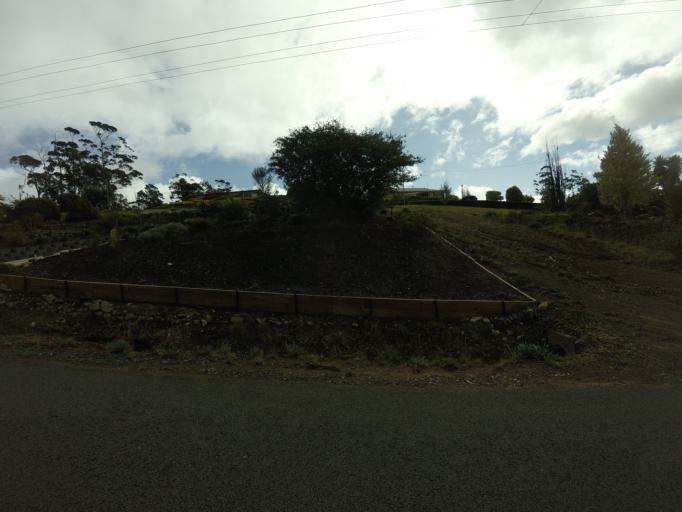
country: AU
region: Tasmania
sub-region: Sorell
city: Sorell
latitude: -42.5393
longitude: 147.9125
